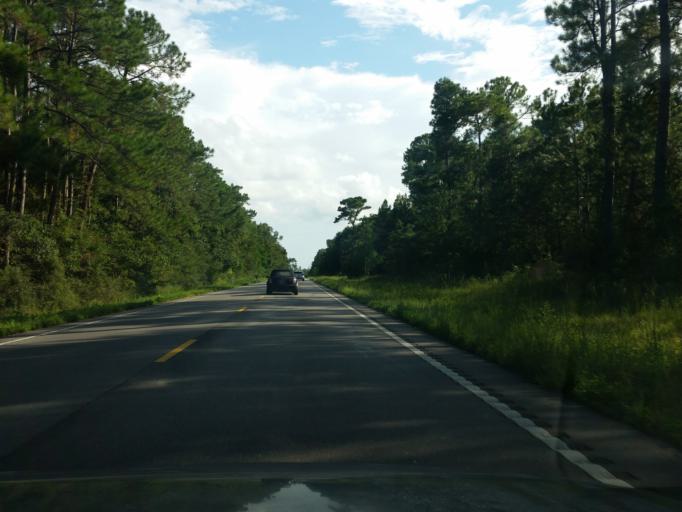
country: US
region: Alabama
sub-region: Mobile County
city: Dauphin Island
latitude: 30.3799
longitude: -88.1089
